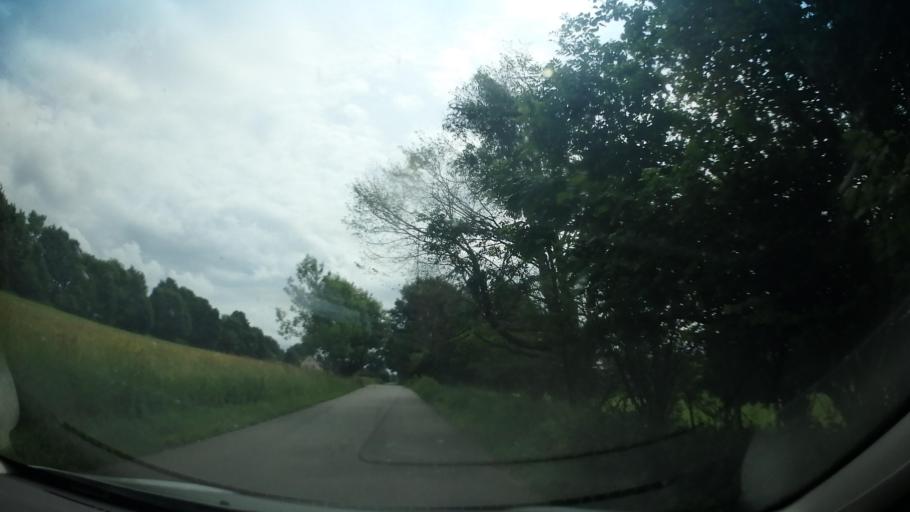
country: CZ
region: Vysocina
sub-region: Okres Zd'ar nad Sazavou
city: Nove Mesto na Morave
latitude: 49.5993
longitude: 16.0630
